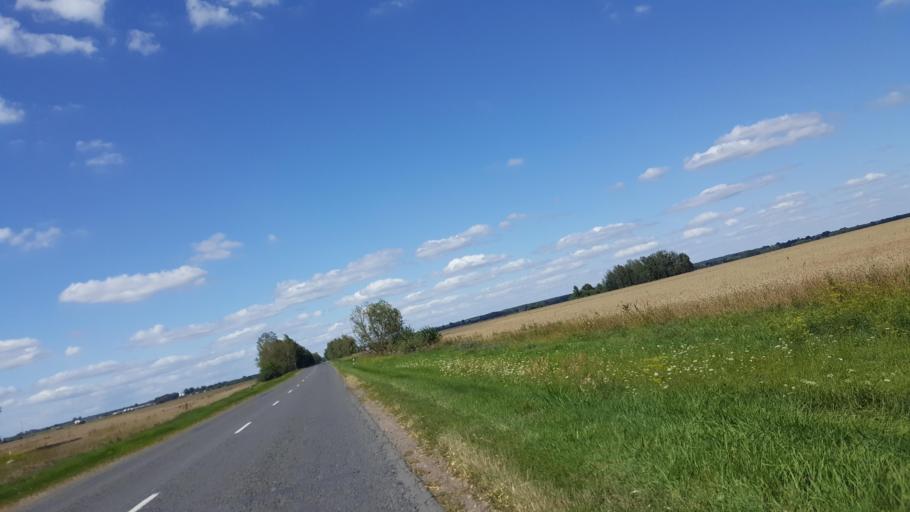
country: BY
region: Brest
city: Kobryn
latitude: 52.3174
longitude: 24.2690
